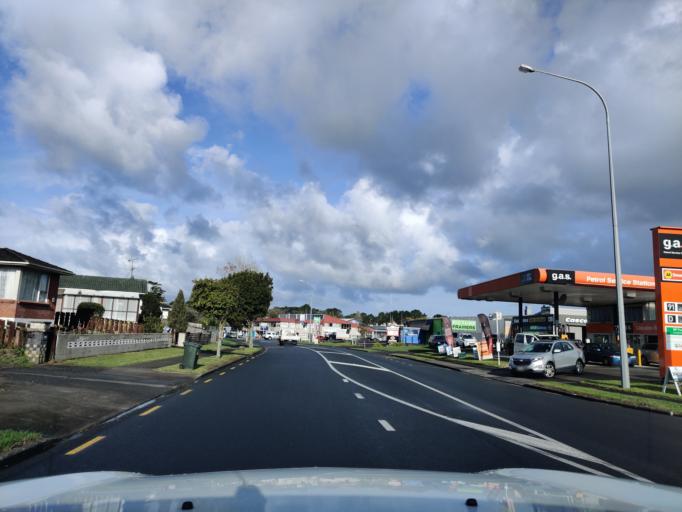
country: NZ
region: Auckland
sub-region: Auckland
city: Pakuranga
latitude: -36.9131
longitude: 174.9022
